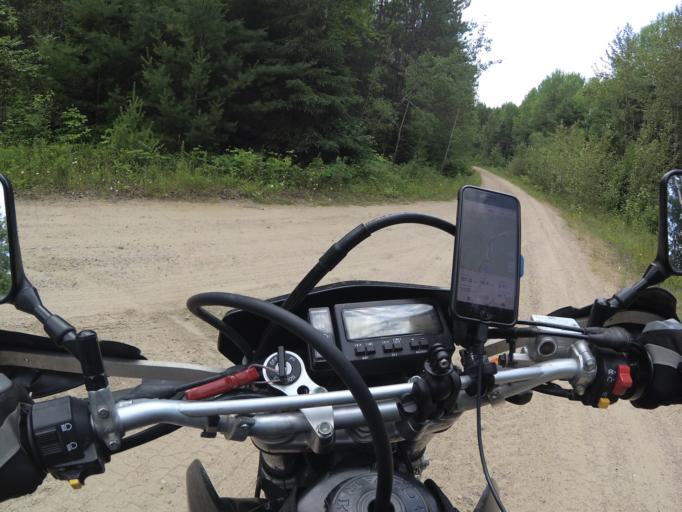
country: CA
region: Ontario
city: Bancroft
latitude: 45.0347
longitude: -77.2640
